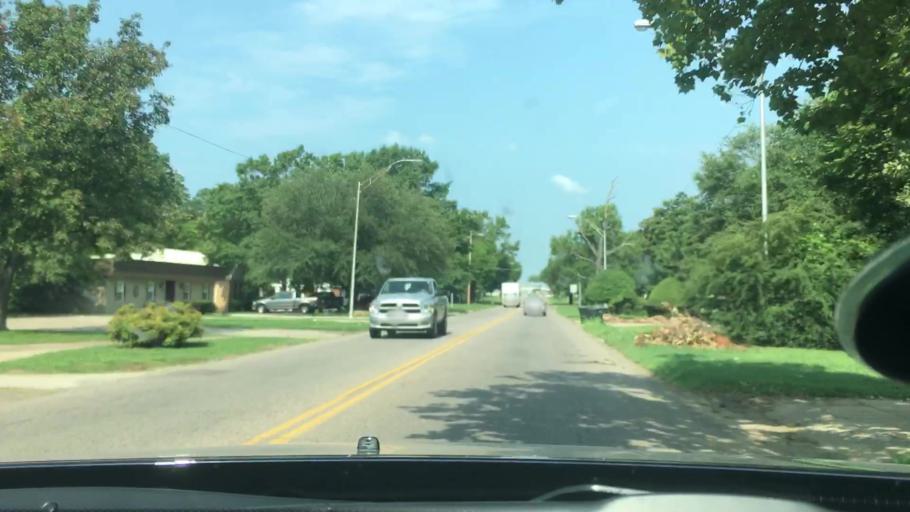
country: US
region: Oklahoma
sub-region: Bryan County
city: Durant
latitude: 33.9957
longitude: -96.3958
